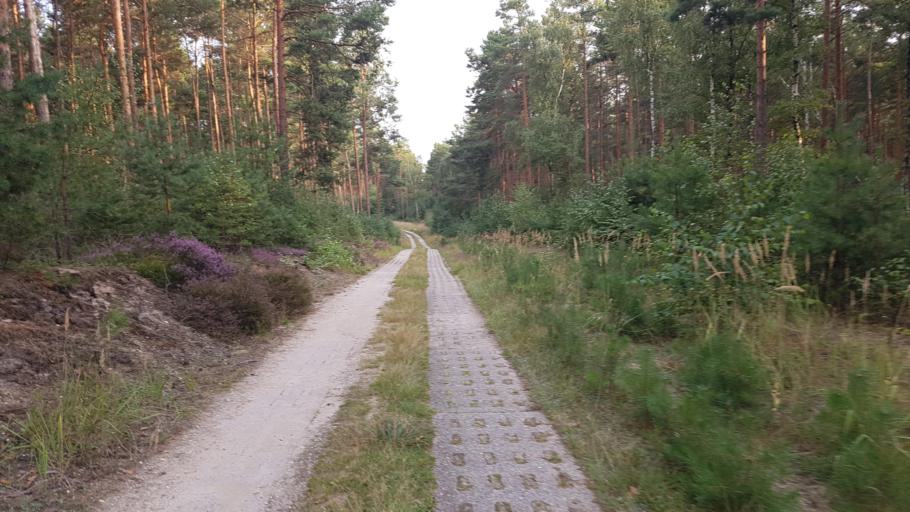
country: DE
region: Brandenburg
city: Schonborn
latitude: 51.6337
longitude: 13.4979
